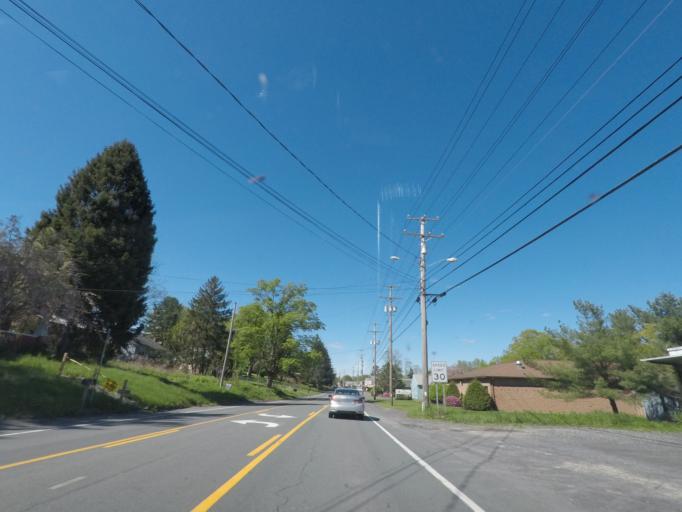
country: US
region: New York
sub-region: Albany County
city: Ravena
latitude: 42.4637
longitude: -73.8172
